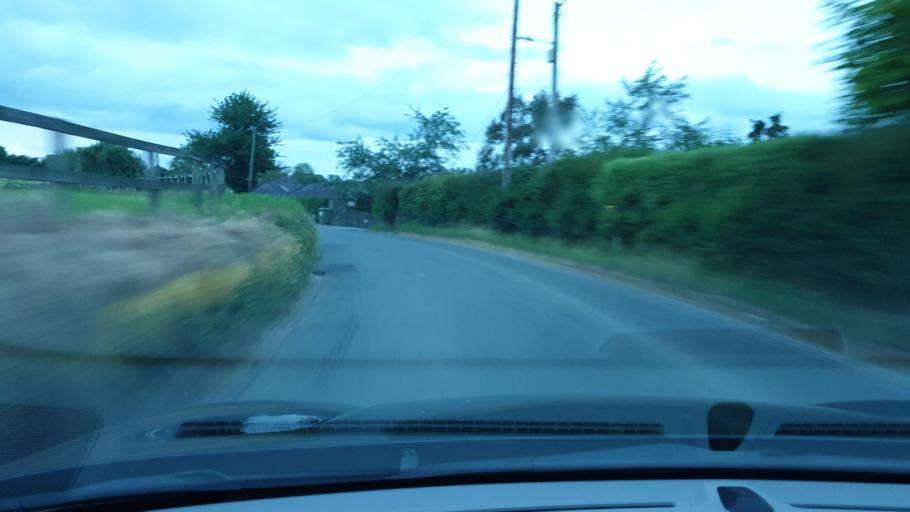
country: IE
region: Leinster
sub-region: An Mhi
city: Ashbourne
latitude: 53.5693
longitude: -6.4006
